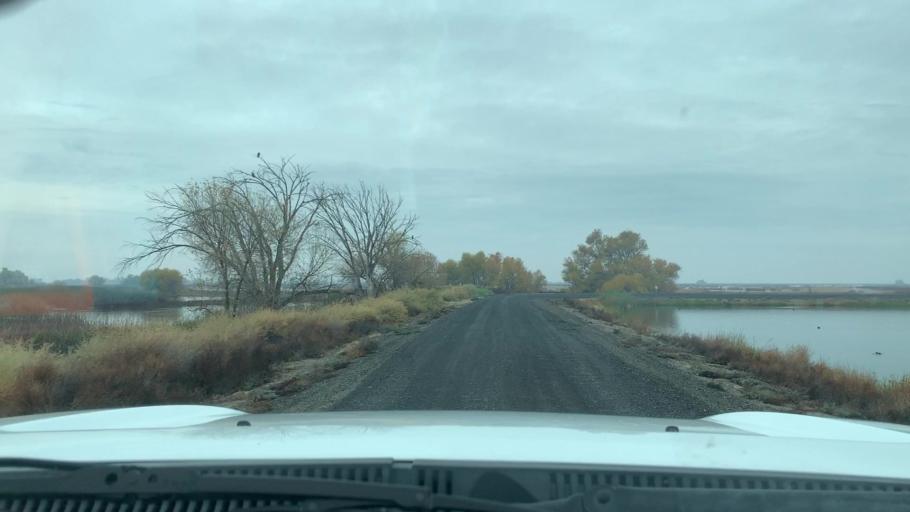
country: US
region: California
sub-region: Kern County
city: Lost Hills
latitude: 35.7488
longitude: -119.5929
